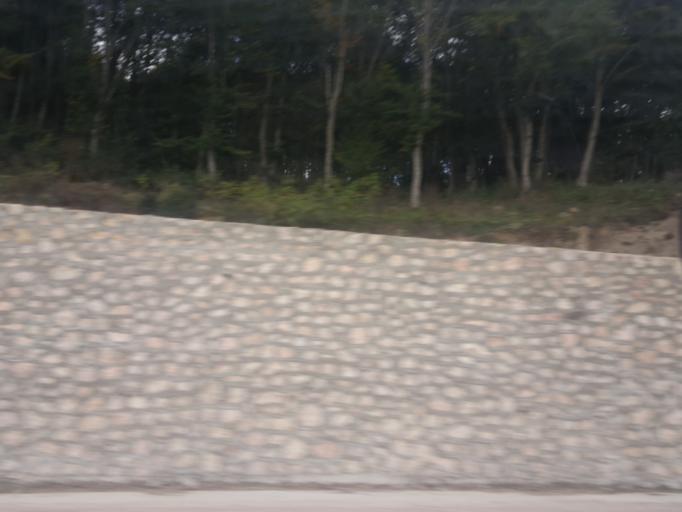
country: TR
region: Tokat
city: Bereketli
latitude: 40.5570
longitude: 37.3109
